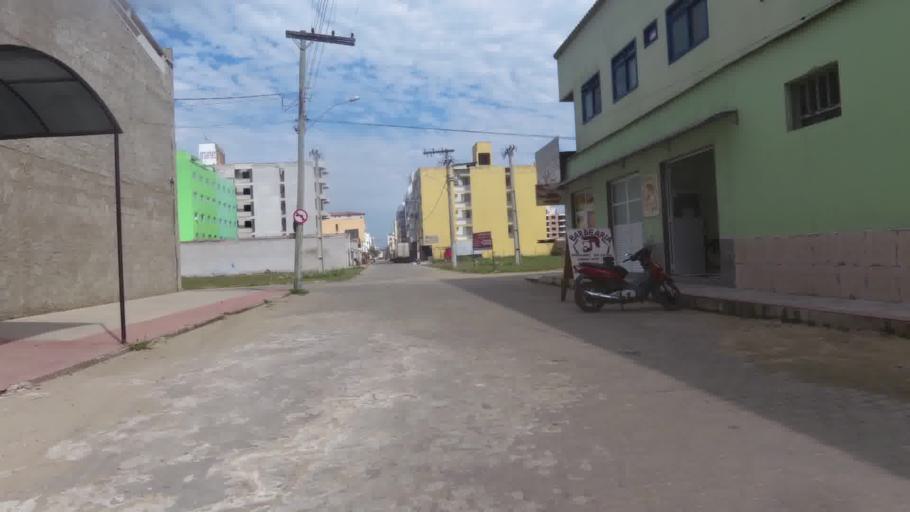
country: BR
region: Espirito Santo
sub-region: Piuma
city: Piuma
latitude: -20.8442
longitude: -40.7377
